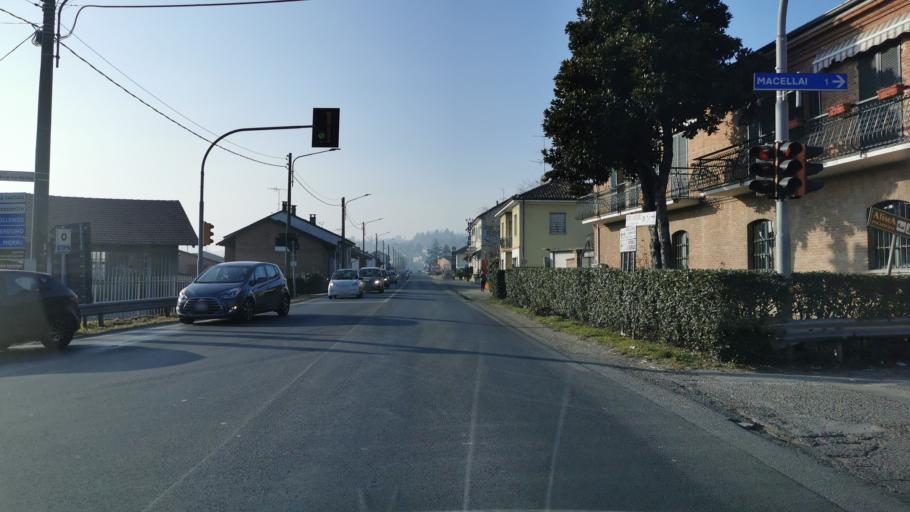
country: IT
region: Piedmont
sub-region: Provincia di Cuneo
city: Pocapaglia
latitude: 44.6973
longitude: 7.8874
